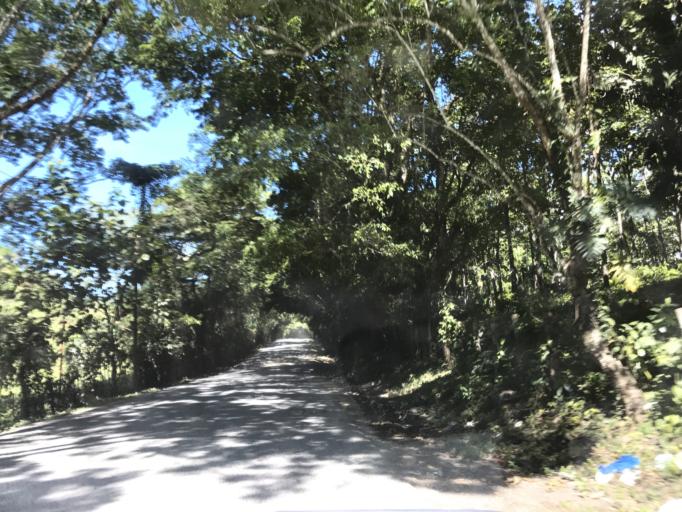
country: GT
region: Izabal
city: Morales
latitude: 15.6481
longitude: -89.0103
